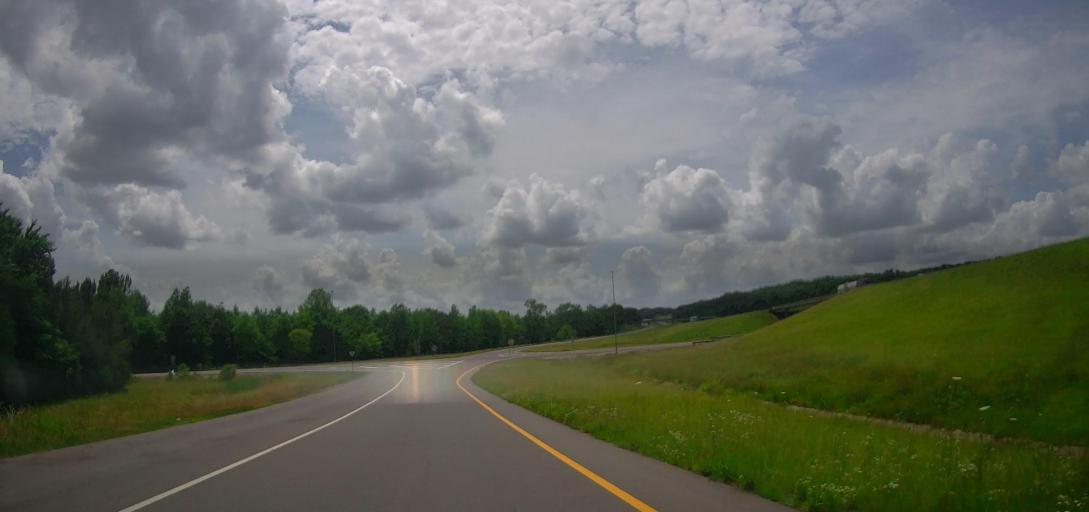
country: US
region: Alabama
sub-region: Marion County
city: Hamilton
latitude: 34.0711
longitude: -87.9737
